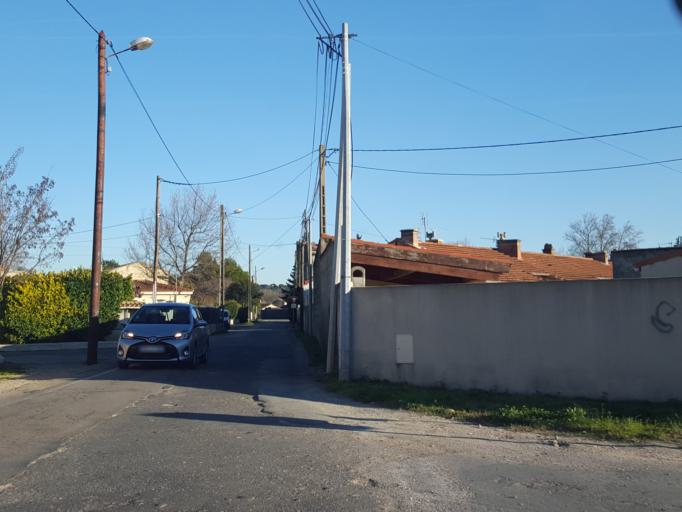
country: FR
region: Provence-Alpes-Cote d'Azur
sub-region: Departement du Vaucluse
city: Sorgues
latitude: 43.9893
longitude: 4.8745
